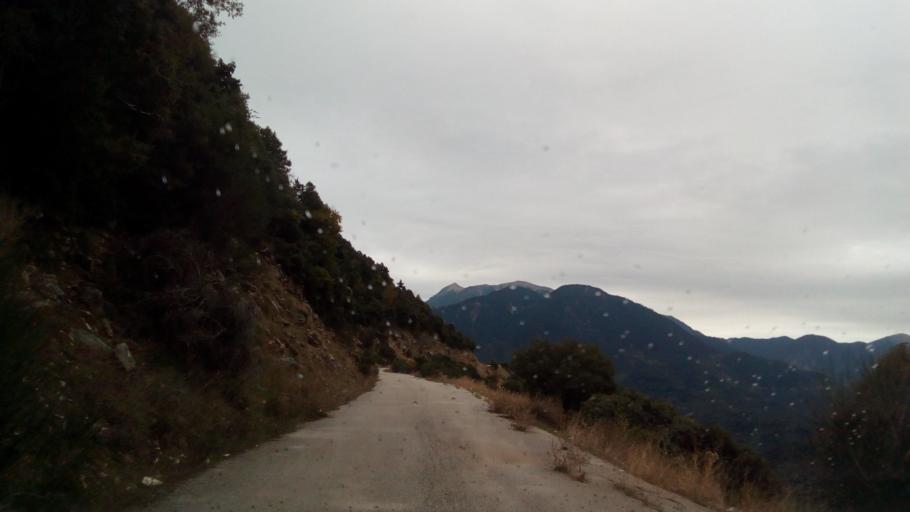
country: GR
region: West Greece
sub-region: Nomos Aitolias kai Akarnanias
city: Thermo
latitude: 38.6170
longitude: 21.8309
